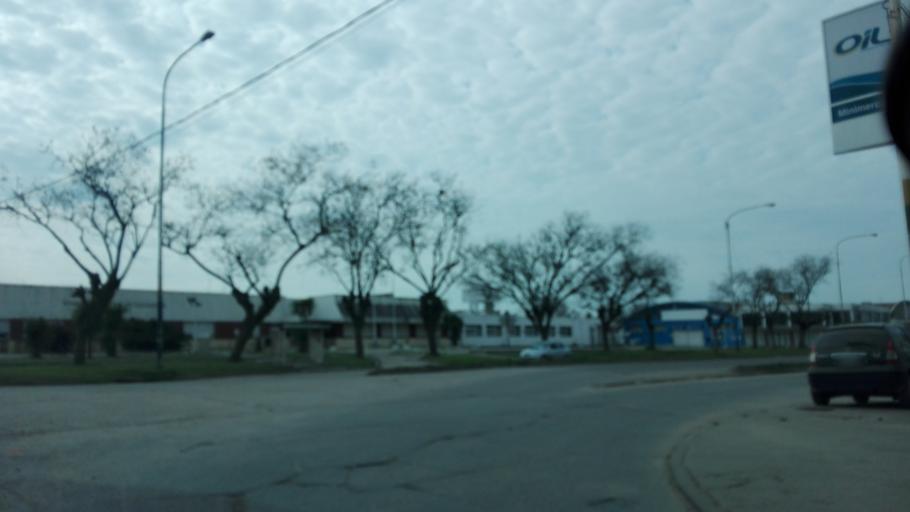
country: AR
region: Buenos Aires
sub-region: Partido de Chascomus
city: Chascomus
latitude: -35.5772
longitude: -58.0082
